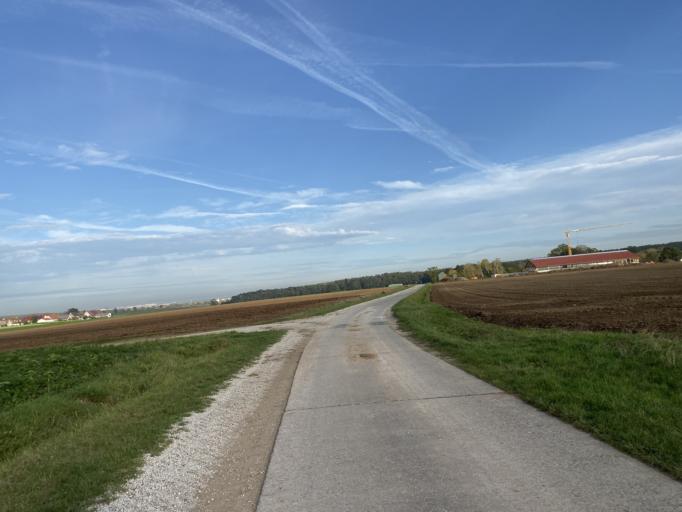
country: DE
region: Bavaria
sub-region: Regierungsbezirk Mittelfranken
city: Puschendorf
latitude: 49.5497
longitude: 10.8345
